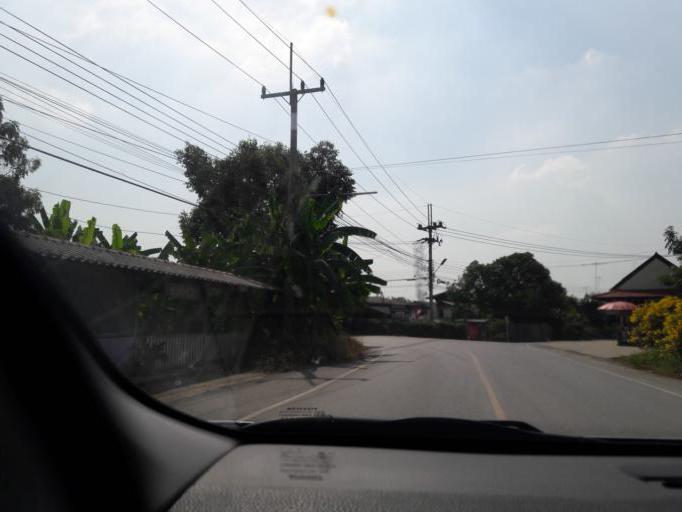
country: TH
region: Ang Thong
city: Ang Thong
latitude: 14.5851
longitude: 100.4292
